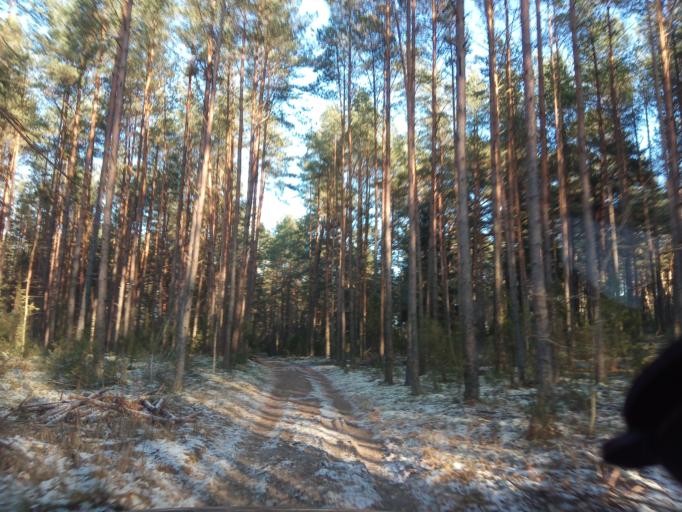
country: LT
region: Alytaus apskritis
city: Druskininkai
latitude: 53.9510
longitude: 23.8827
